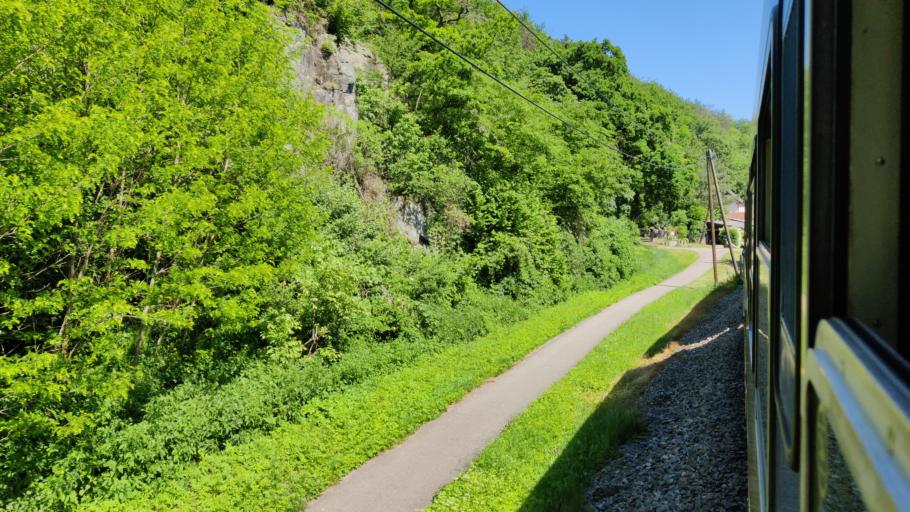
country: AT
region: Lower Austria
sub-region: Politischer Bezirk Horn
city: Gars am Kamp
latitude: 48.6039
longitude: 15.6534
